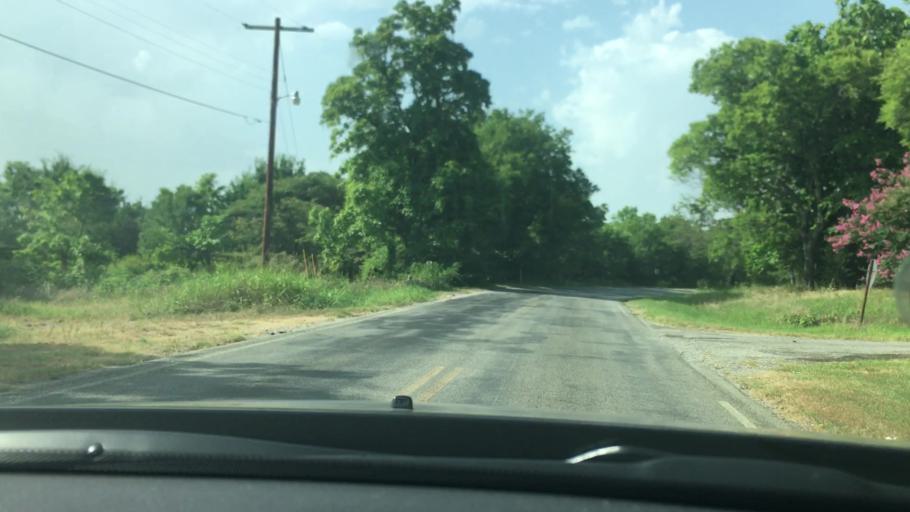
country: US
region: Oklahoma
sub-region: Pontotoc County
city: Byng
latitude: 34.8718
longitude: -96.5961
